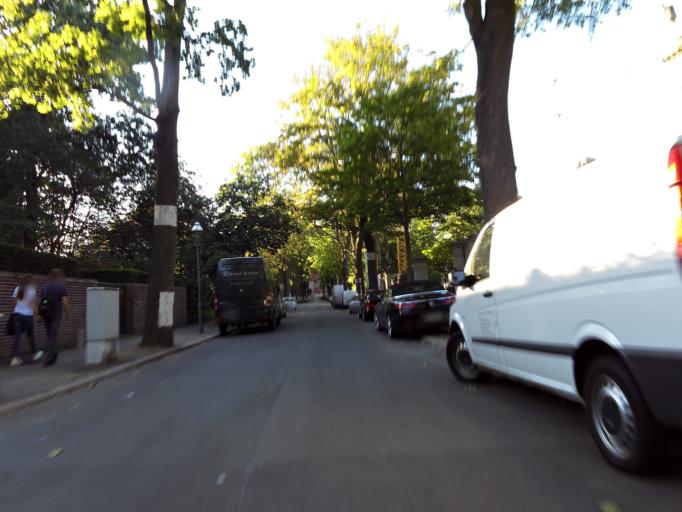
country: DE
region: Berlin
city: Grunewald
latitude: 52.4841
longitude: 13.2627
